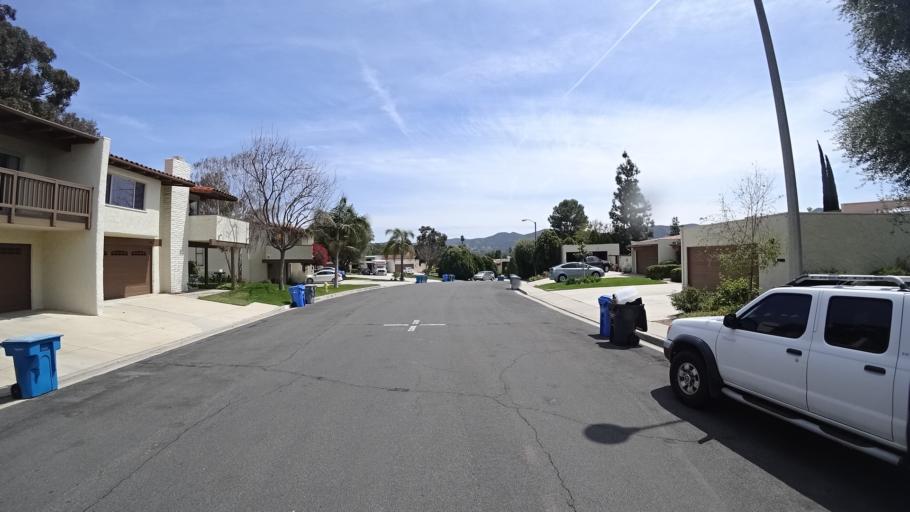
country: US
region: California
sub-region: Ventura County
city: Casa Conejo
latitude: 34.1894
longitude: -118.8908
